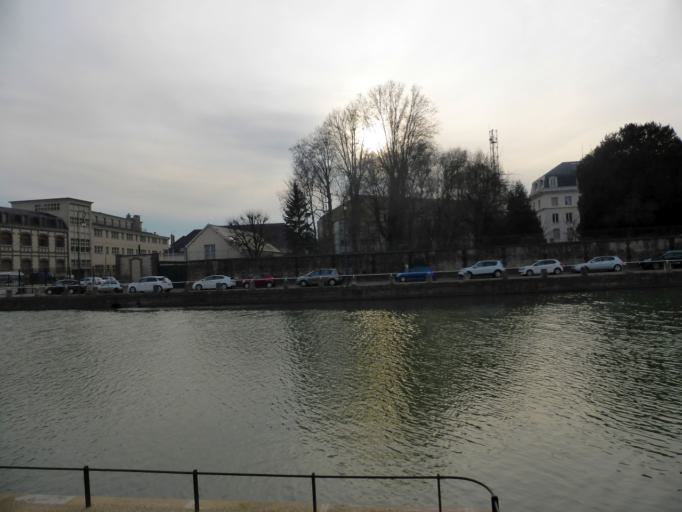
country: FR
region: Champagne-Ardenne
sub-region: Departement de l'Aube
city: Troyes
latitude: 48.2976
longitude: 4.0801
